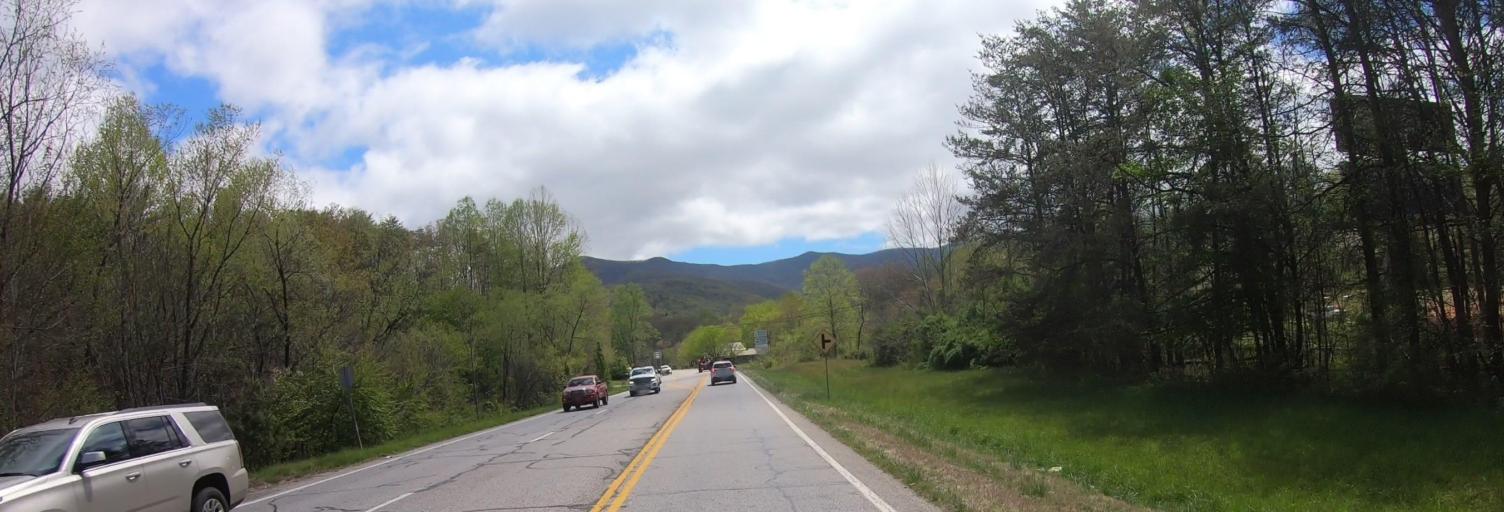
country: US
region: Georgia
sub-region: Union County
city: Blairsville
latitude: 34.9101
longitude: -83.8698
